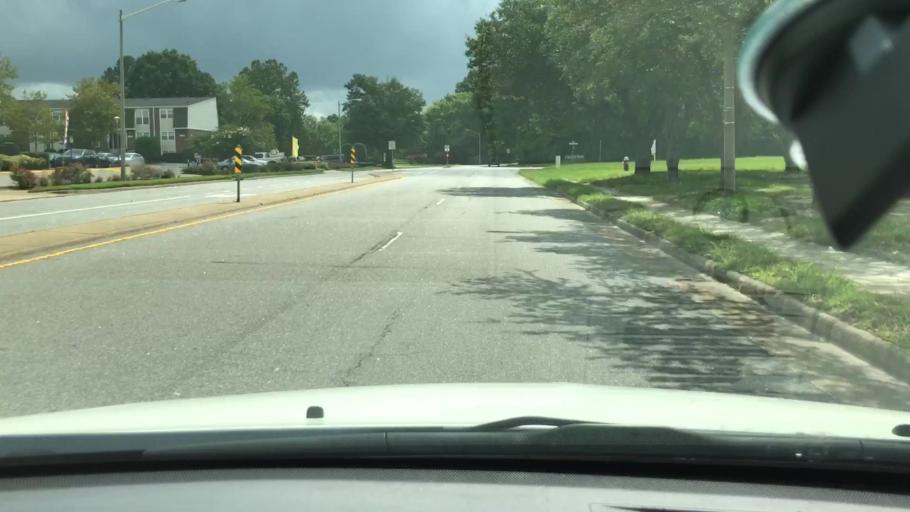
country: US
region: Virginia
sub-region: City of Chesapeake
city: Chesapeake
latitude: 36.8109
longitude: -76.2138
